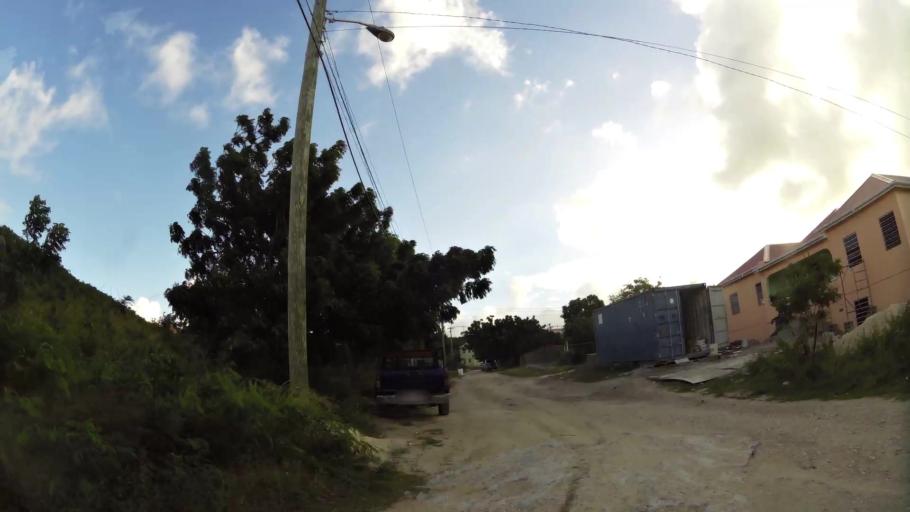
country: AG
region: Saint John
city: Saint John's
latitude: 17.1573
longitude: -61.8229
